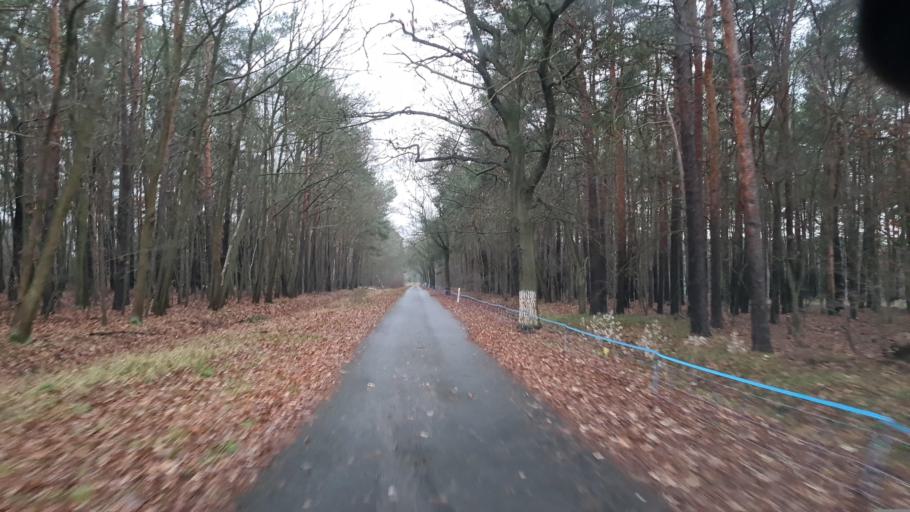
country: DE
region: Brandenburg
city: Neupetershain
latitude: 51.6338
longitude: 14.1838
